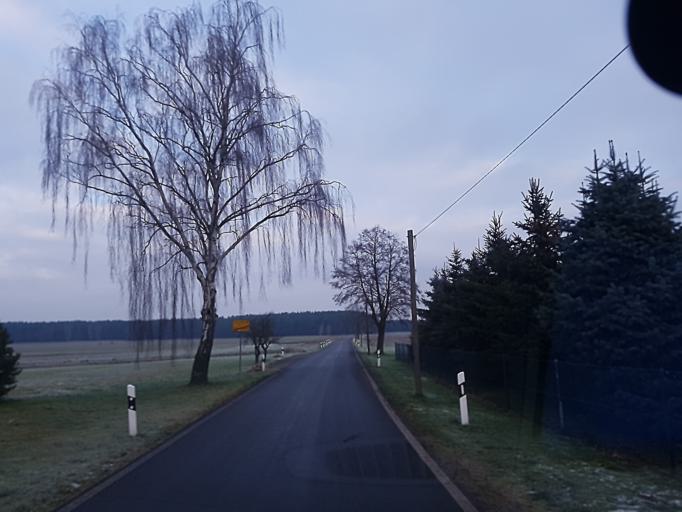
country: DE
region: Brandenburg
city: Crinitz
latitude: 51.7351
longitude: 13.8303
